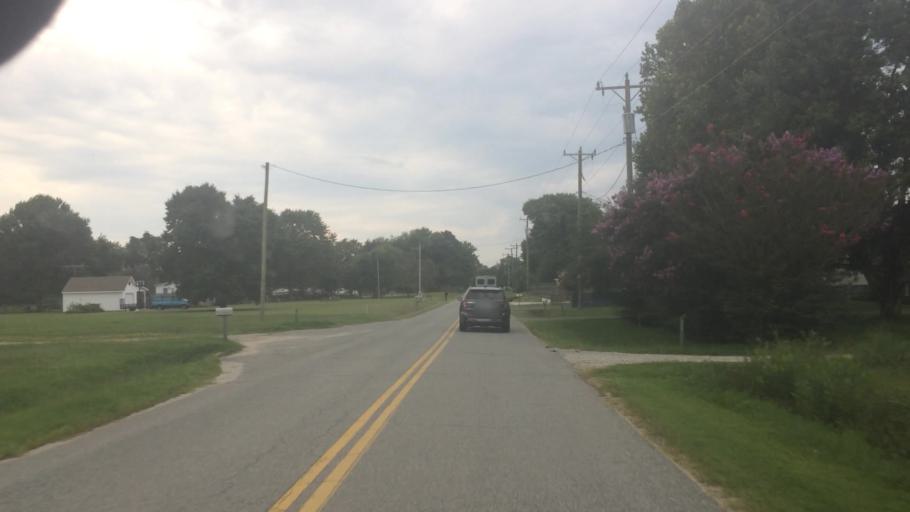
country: US
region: Virginia
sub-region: King William County
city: West Point
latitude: 37.5509
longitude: -76.7164
